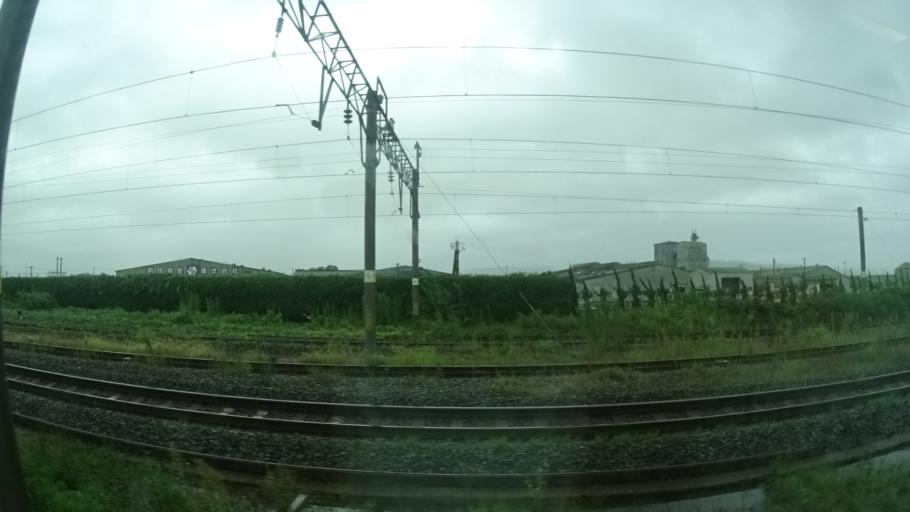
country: JP
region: Yamagata
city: Sakata
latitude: 38.8435
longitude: 139.9120
